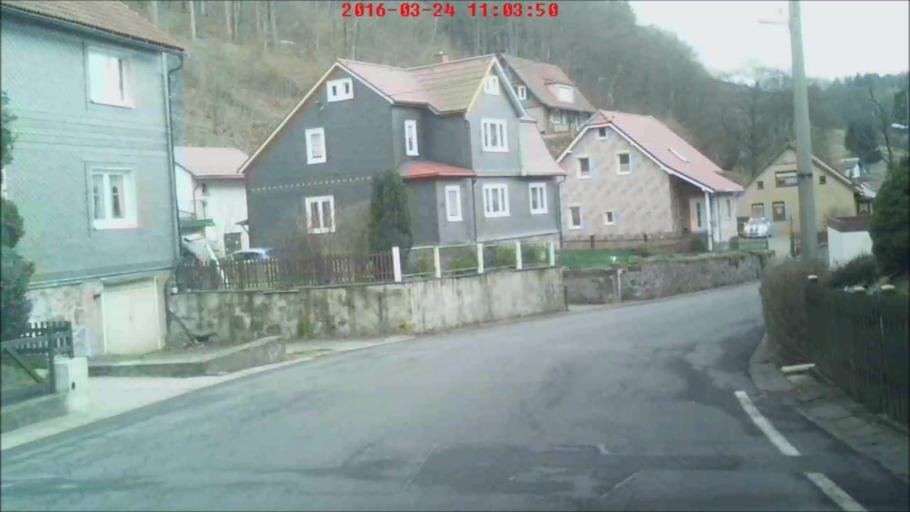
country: DE
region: Thuringia
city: Neustadt am Rennsteig
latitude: 50.5433
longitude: 10.9205
